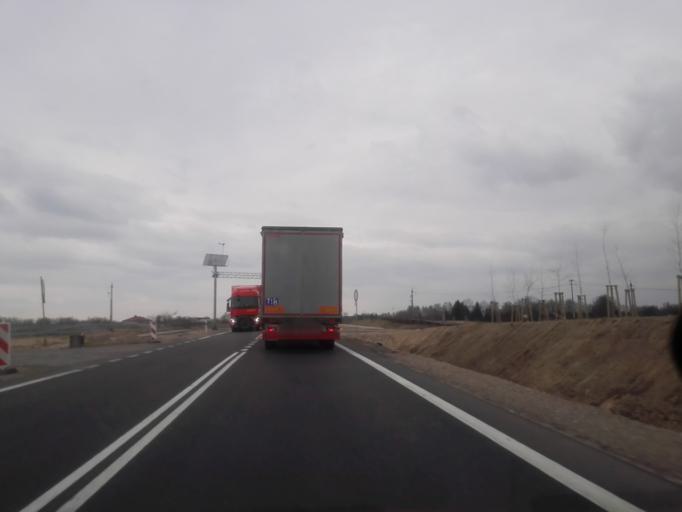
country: PL
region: Podlasie
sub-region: Powiat augustowski
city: Augustow
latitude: 53.7858
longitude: 22.8523
